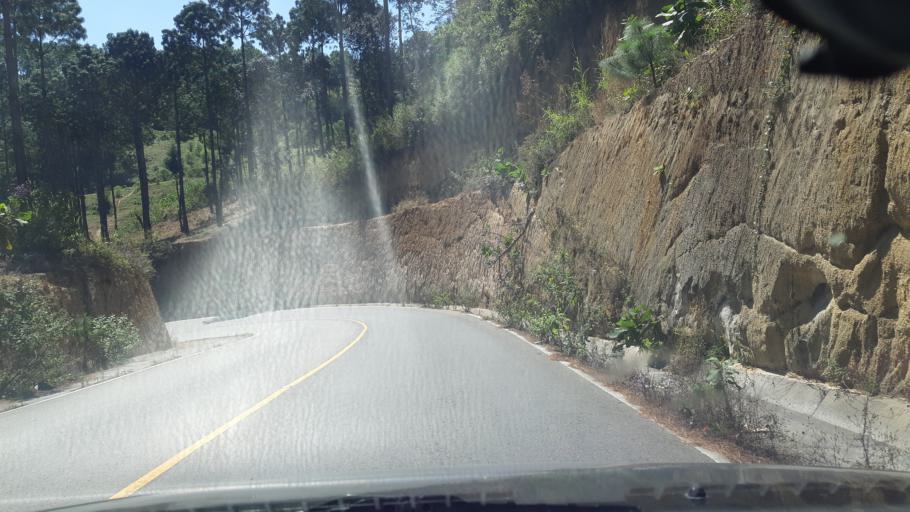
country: GT
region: Chimaltenango
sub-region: Municipio de Zaragoza
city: Zaragoza
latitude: 14.6660
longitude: -90.8598
